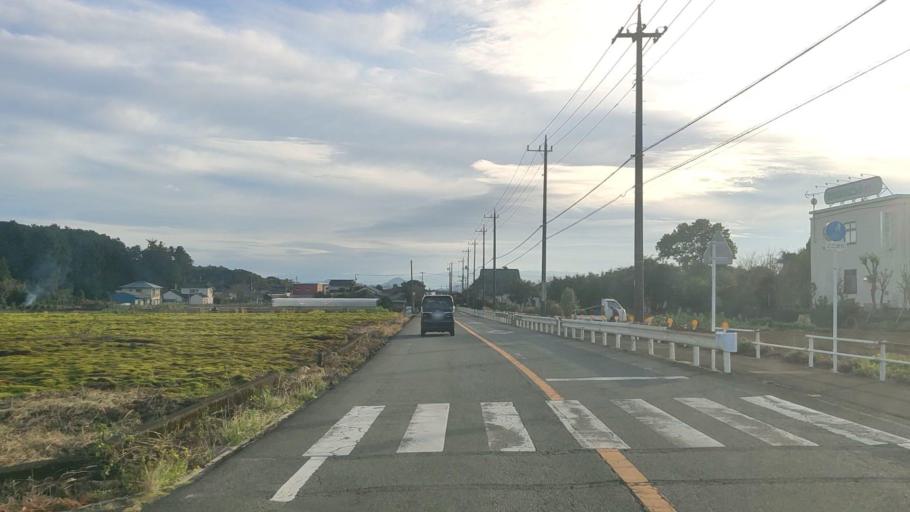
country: JP
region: Shizuoka
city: Mishima
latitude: 35.1857
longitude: 138.9208
